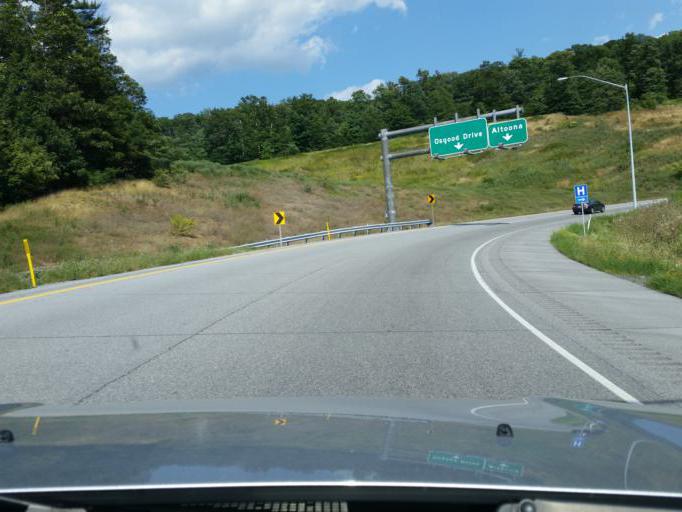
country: US
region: Pennsylvania
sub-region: Blair County
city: Lakemont
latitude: 40.4949
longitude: -78.3810
